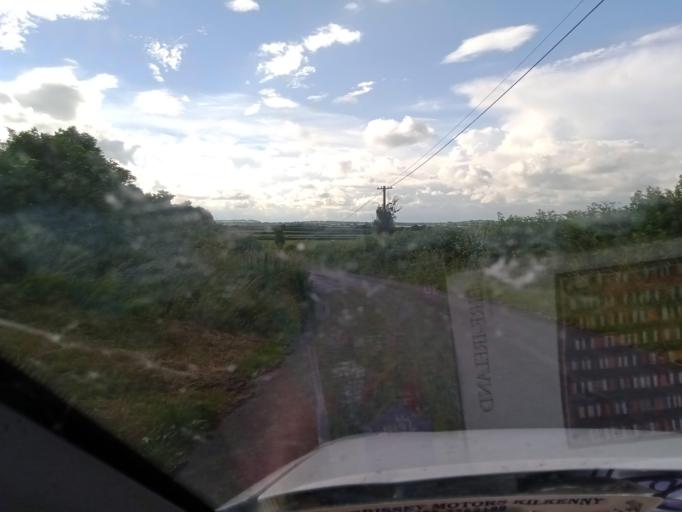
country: IE
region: Leinster
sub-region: Laois
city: Rathdowney
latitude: 52.7738
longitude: -7.5166
